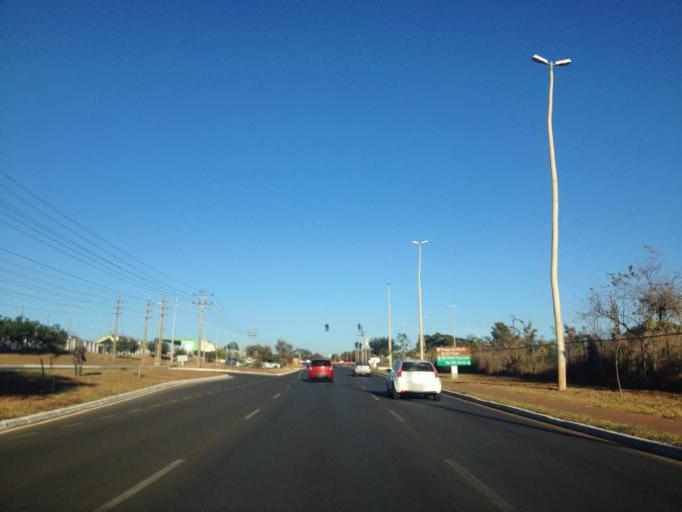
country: BR
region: Federal District
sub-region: Brasilia
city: Brasilia
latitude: -15.7705
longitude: -47.8966
